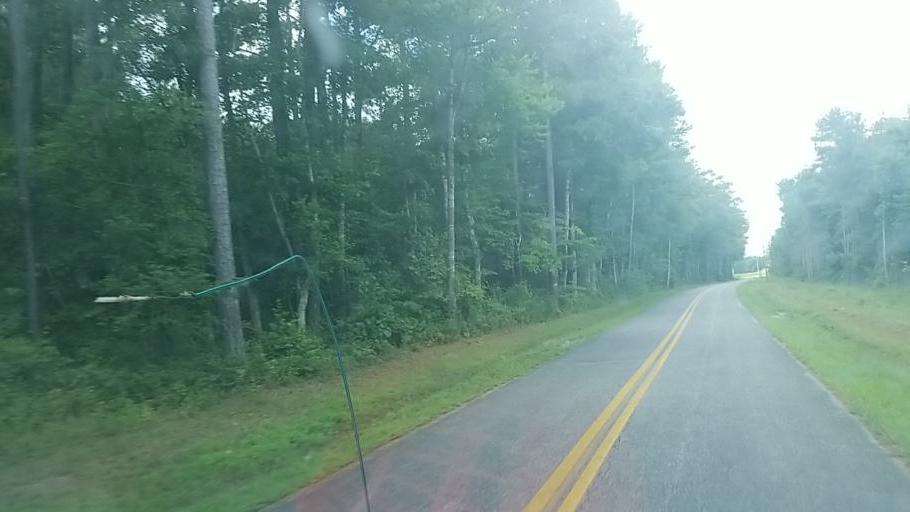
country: US
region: Maryland
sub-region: Worcester County
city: Snow Hill
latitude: 38.2580
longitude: -75.4467
